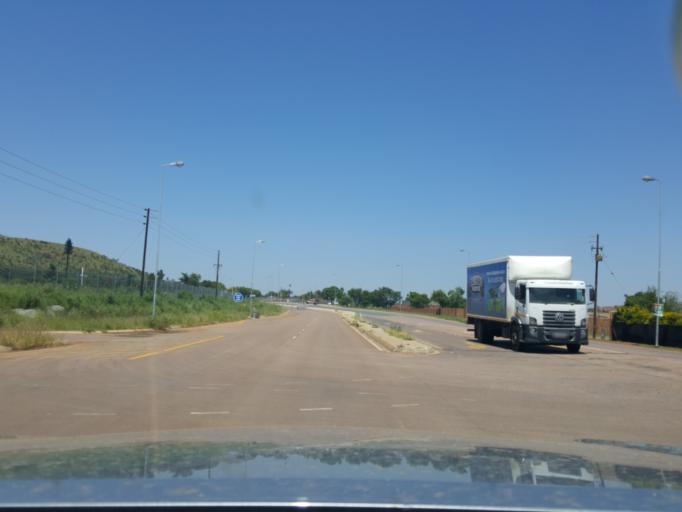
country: ZA
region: Gauteng
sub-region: City of Tshwane Metropolitan Municipality
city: Pretoria
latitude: -25.6803
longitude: 28.2999
